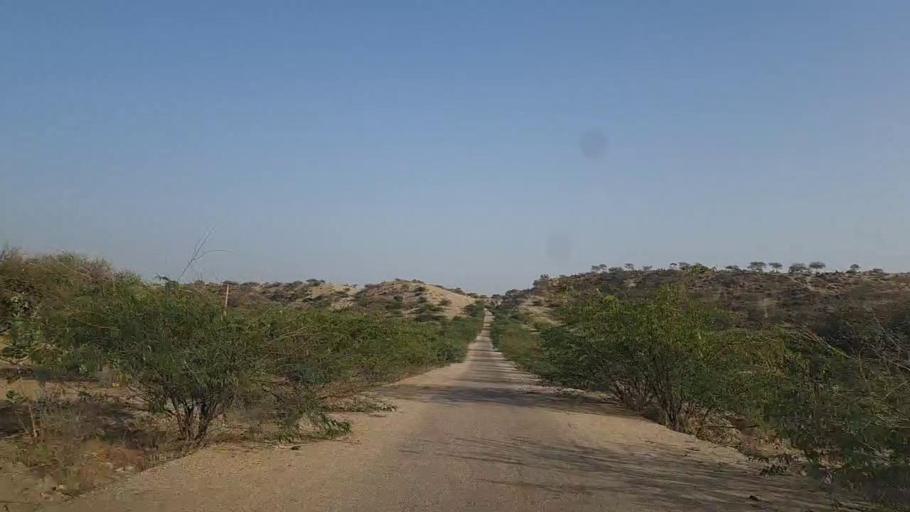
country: PK
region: Sindh
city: Diplo
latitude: 24.5991
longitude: 69.3836
